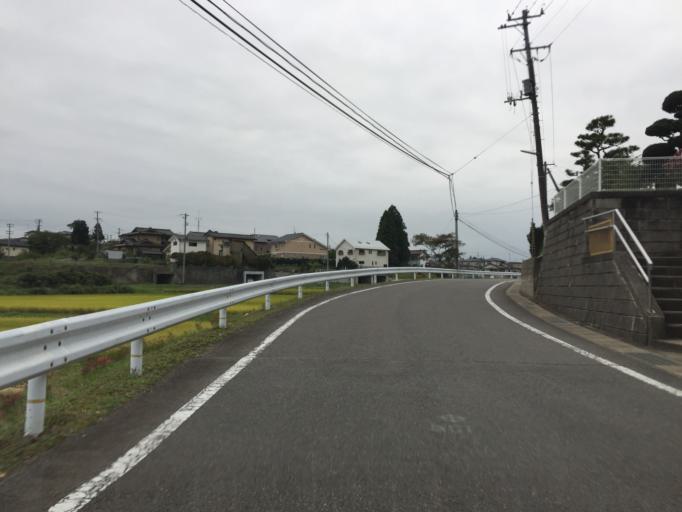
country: JP
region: Fukushima
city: Nihommatsu
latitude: 37.6601
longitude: 140.4769
